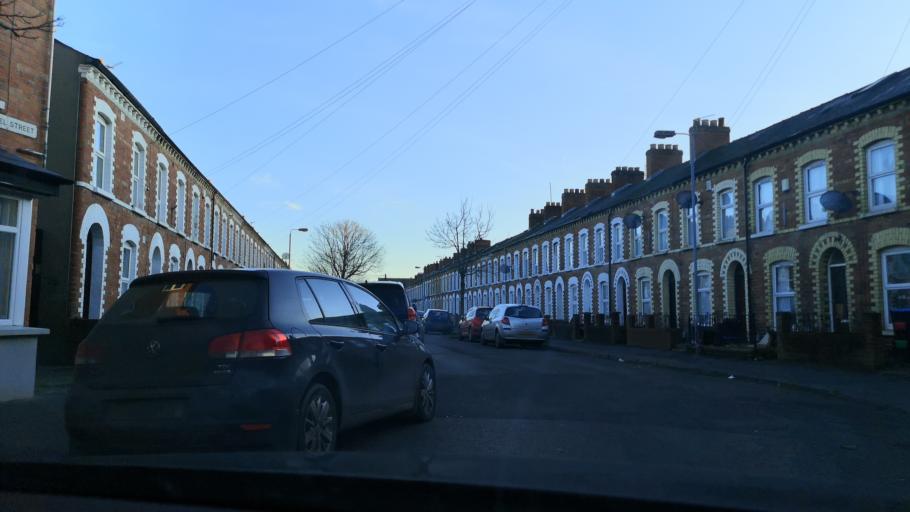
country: GB
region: Northern Ireland
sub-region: City of Belfast
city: Belfast
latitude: 54.5841
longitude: -5.9284
